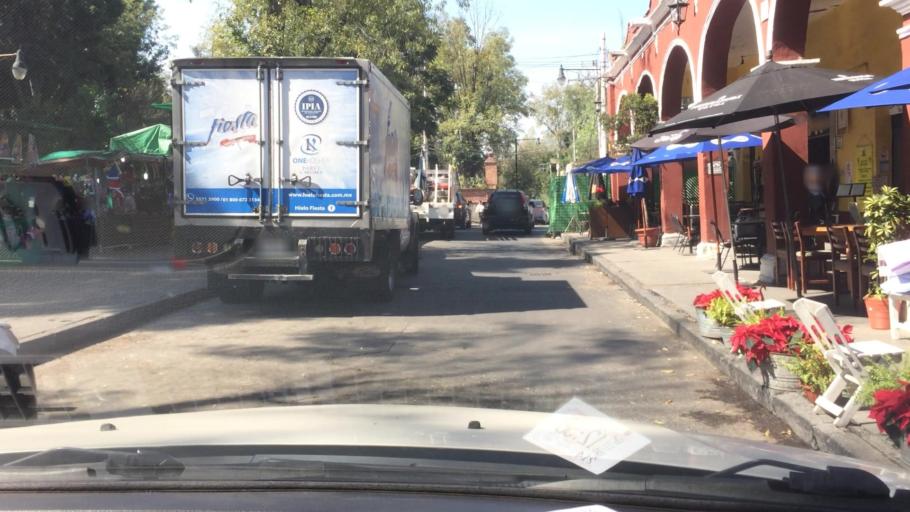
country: MX
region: Mexico City
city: Tlalpan
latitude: 19.2890
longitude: -99.1667
